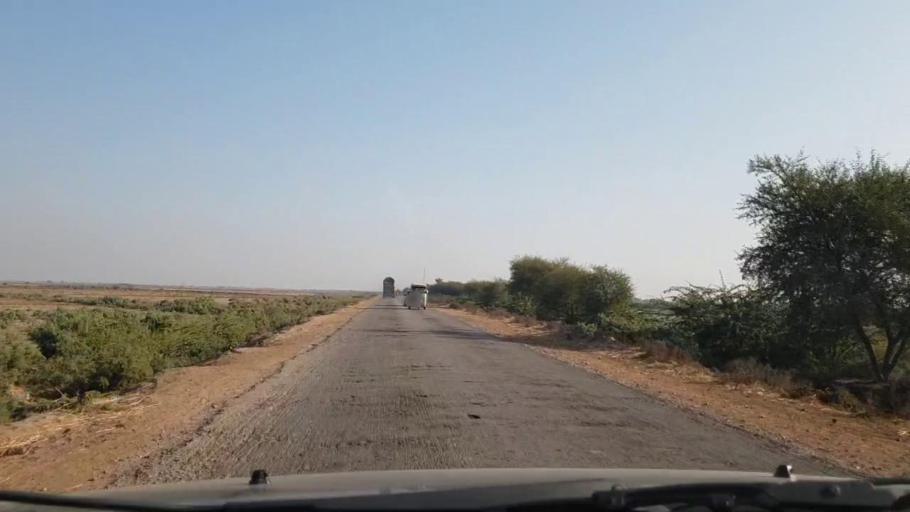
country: PK
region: Sindh
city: Tando Bago
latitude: 24.8329
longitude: 69.0189
